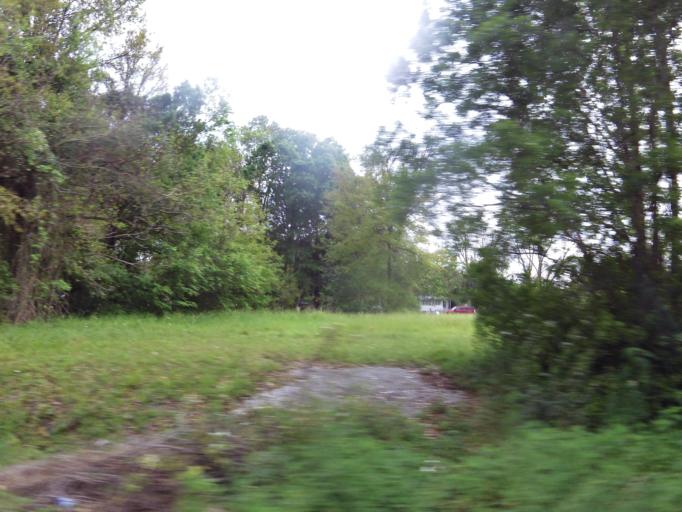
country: US
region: Florida
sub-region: Duval County
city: Jacksonville
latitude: 30.3246
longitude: -81.7238
